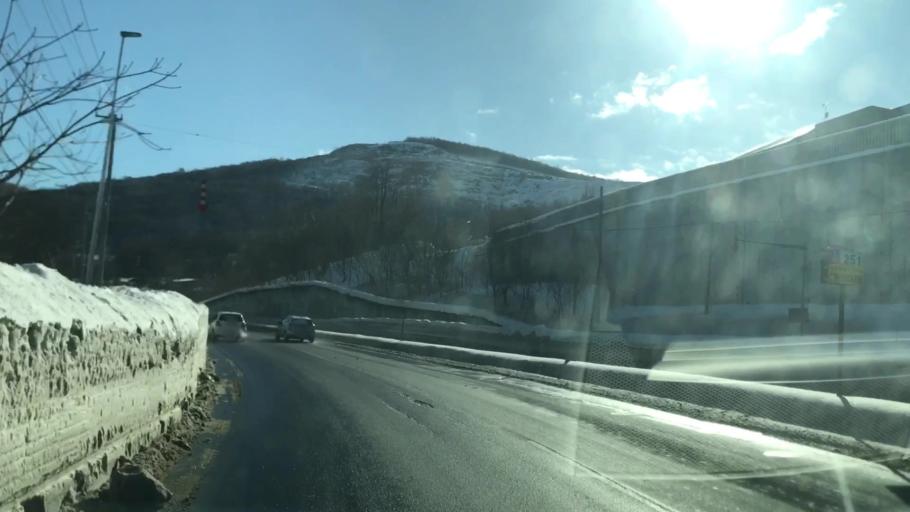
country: JP
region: Hokkaido
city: Otaru
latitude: 43.1730
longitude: 141.0700
